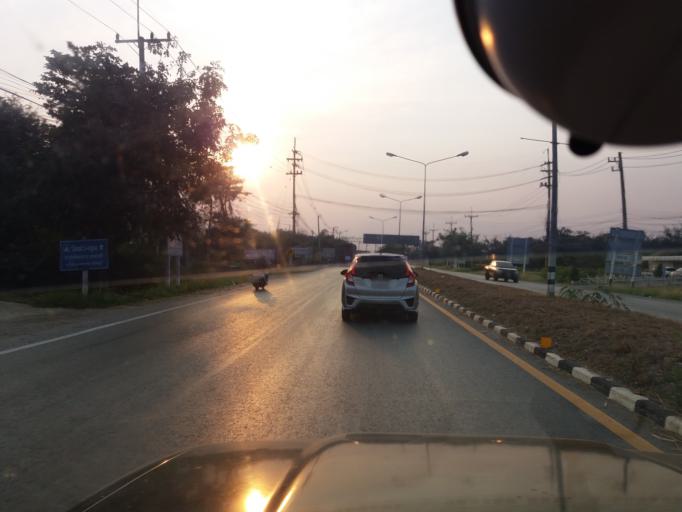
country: TH
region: Sing Buri
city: Sing Buri
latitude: 14.8858
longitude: 100.3899
